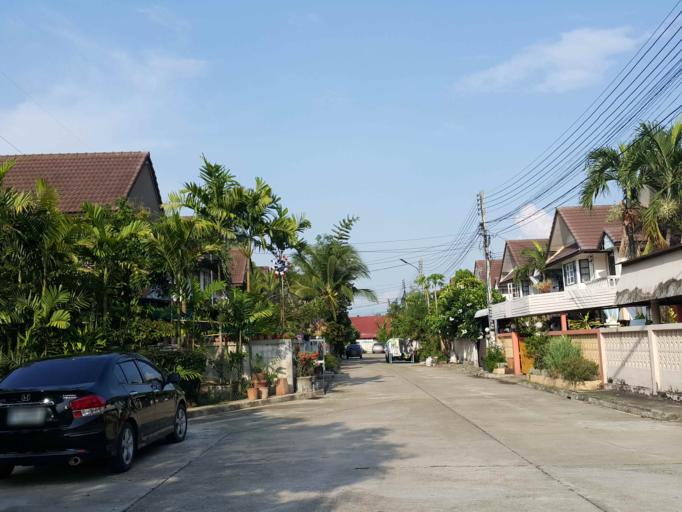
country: TH
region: Chiang Mai
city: San Sai
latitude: 18.8176
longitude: 99.0227
